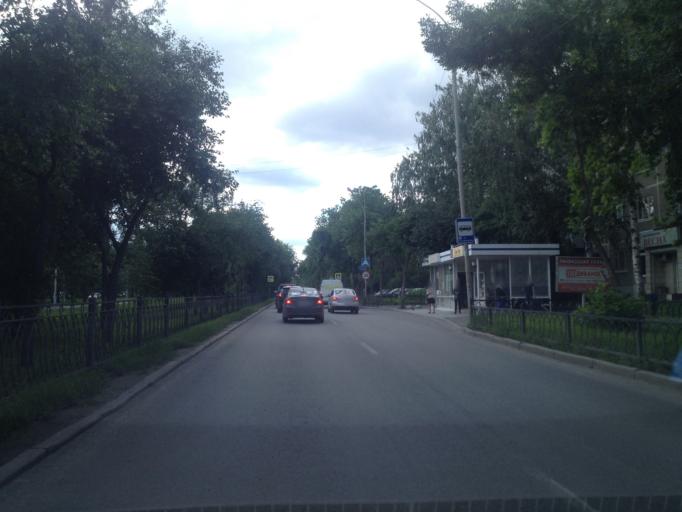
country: RU
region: Sverdlovsk
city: Yekaterinburg
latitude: 56.8179
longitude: 60.5845
